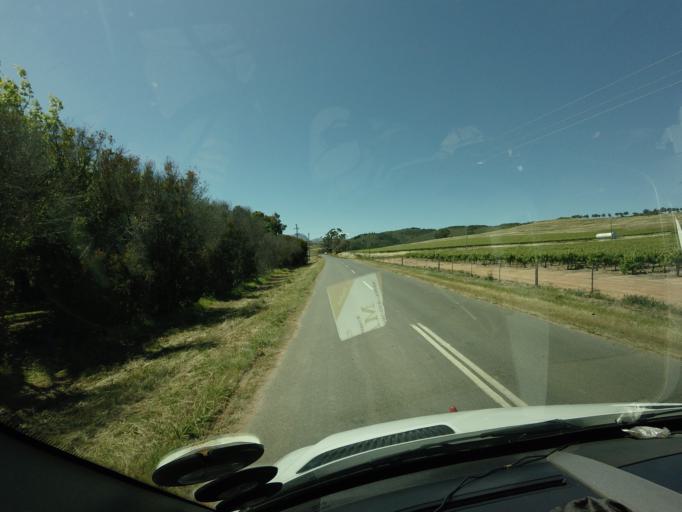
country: ZA
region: Western Cape
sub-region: Cape Winelands District Municipality
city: Stellenbosch
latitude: -33.8724
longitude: 18.8543
